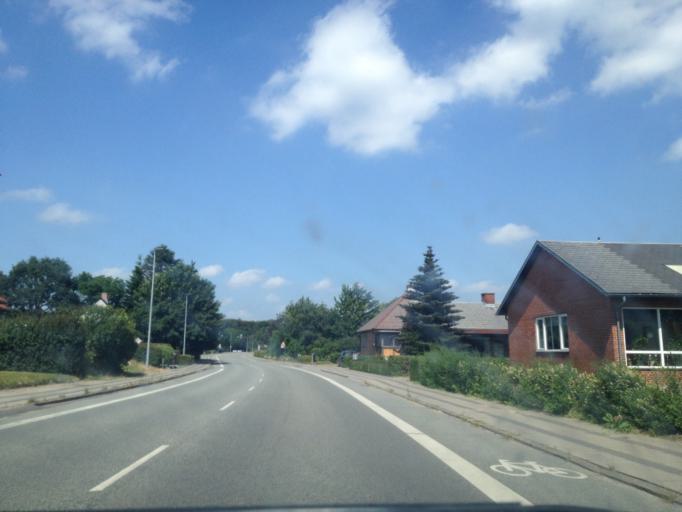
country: DK
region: South Denmark
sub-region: Kolding Kommune
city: Vamdrup
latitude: 55.4305
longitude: 9.2885
